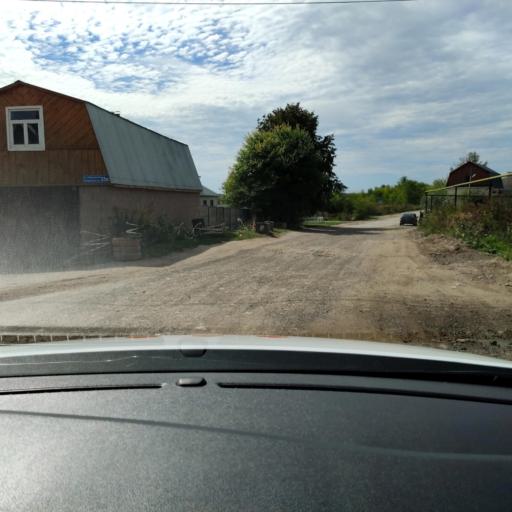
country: RU
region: Tatarstan
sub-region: Gorod Kazan'
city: Kazan
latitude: 55.7151
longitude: 49.0894
